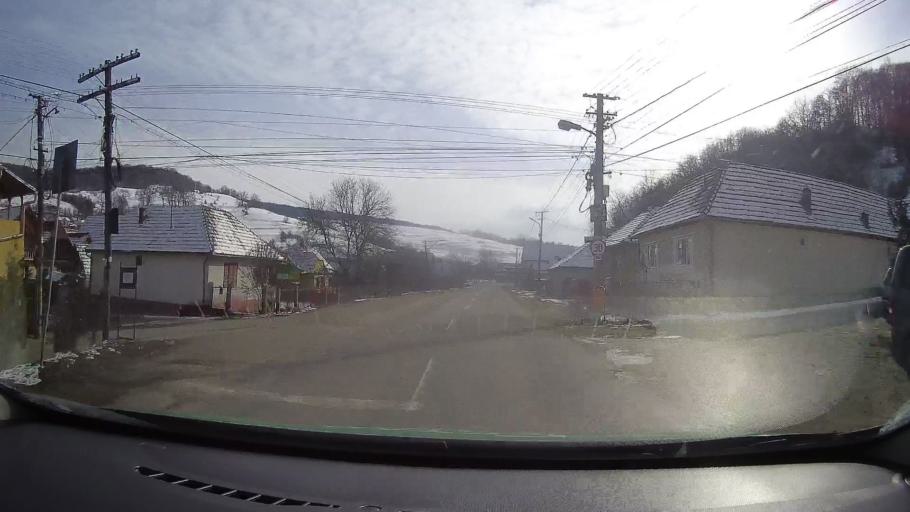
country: RO
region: Mures
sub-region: Municipiul Sighisoara
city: Sighisoara
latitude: 46.2067
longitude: 24.7780
